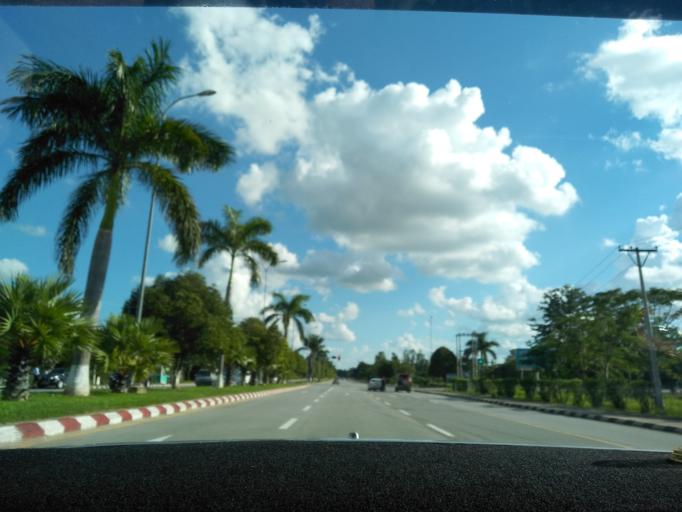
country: MM
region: Mandalay
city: Nay Pyi Taw
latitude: 19.7289
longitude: 96.1111
